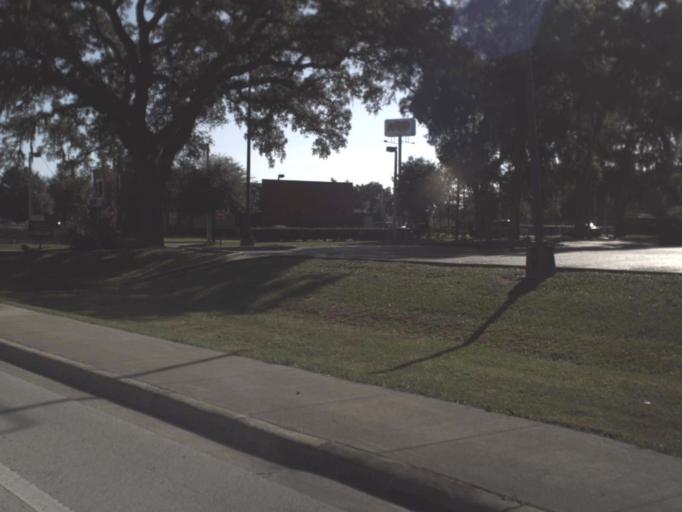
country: US
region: Florida
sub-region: Marion County
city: Belleview
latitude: 29.0254
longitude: -82.1555
